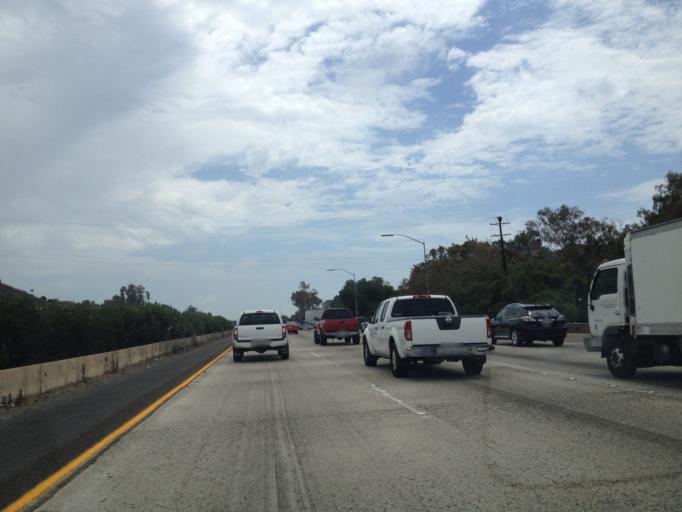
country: US
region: California
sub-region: San Diego County
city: Encinitas
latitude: 33.0814
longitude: -117.2972
